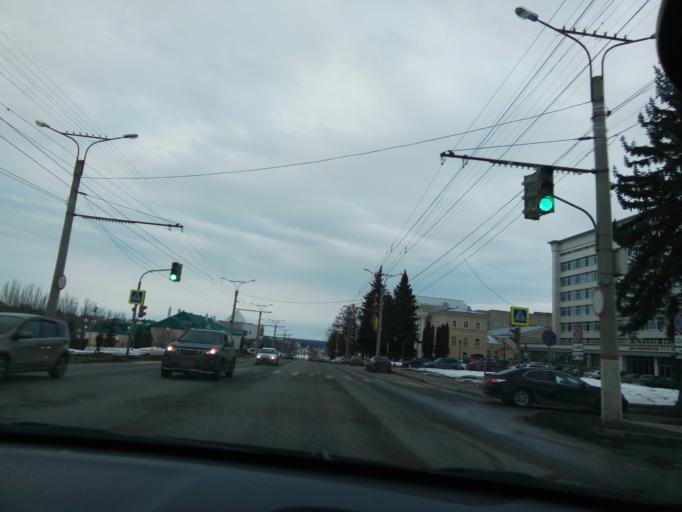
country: RU
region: Chuvashia
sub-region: Cheboksarskiy Rayon
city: Cheboksary
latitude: 56.1398
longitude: 47.2440
